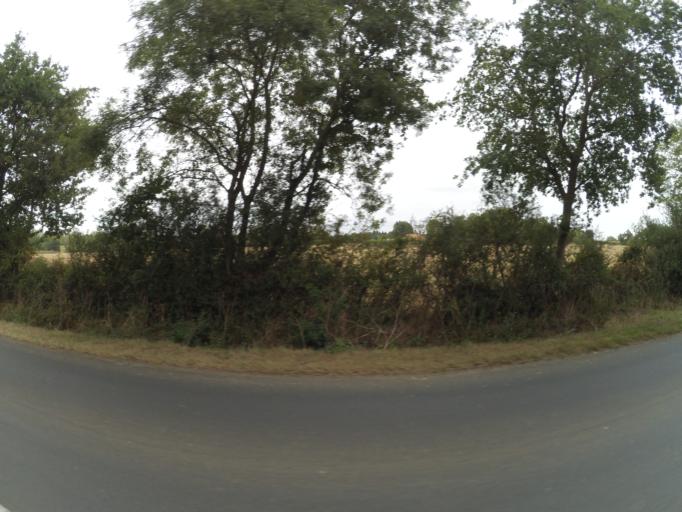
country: FR
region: Pays de la Loire
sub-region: Departement de la Vendee
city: Saint-Andre-Treize-Voies
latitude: 46.9269
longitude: -1.3994
